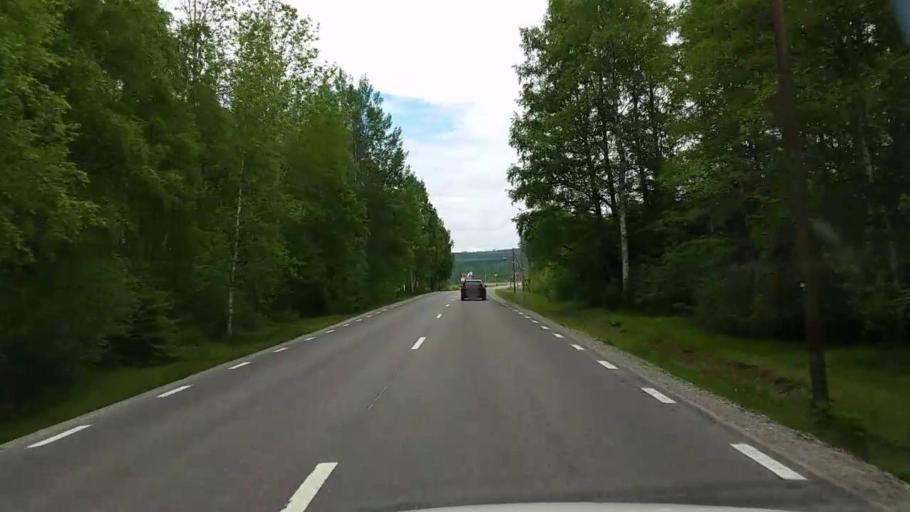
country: SE
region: Gaevleborg
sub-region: Sandvikens Kommun
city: Jarbo
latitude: 60.9597
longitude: 16.4196
